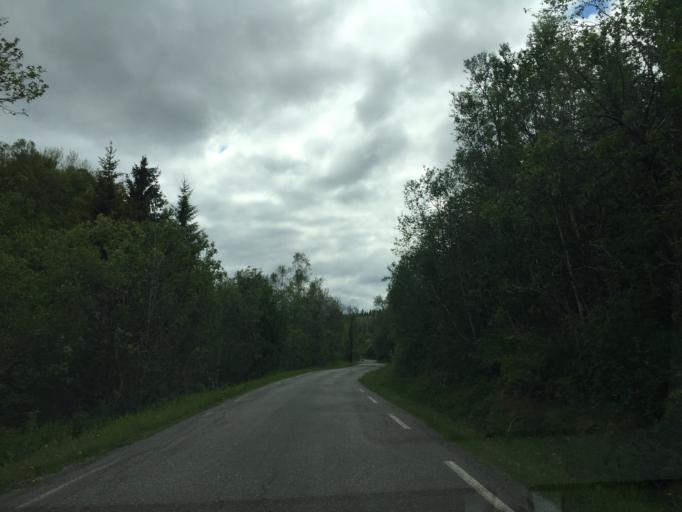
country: NO
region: Nordland
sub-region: Bodo
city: Loding
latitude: 67.3107
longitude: 14.6408
